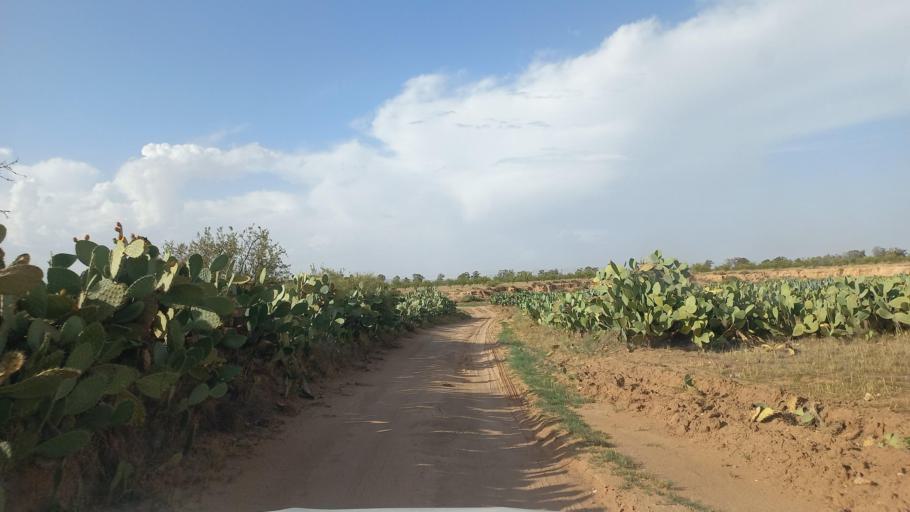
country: TN
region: Al Qasrayn
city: Kasserine
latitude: 35.2276
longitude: 8.9678
